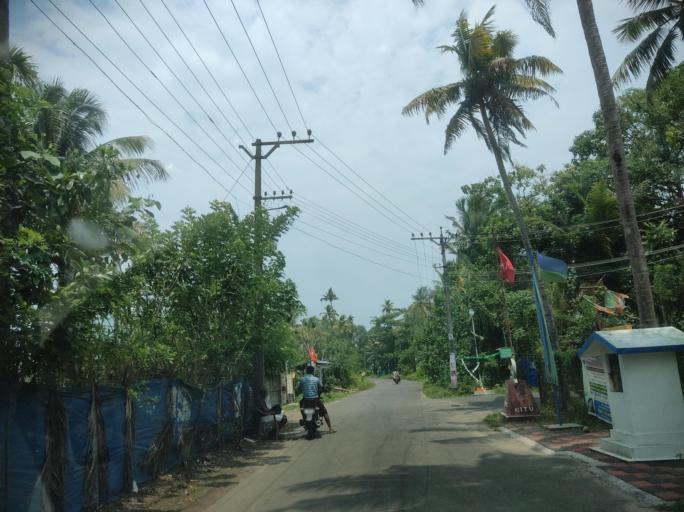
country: IN
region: Kerala
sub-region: Alappuzha
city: Vayalar
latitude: 9.7456
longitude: 76.3251
